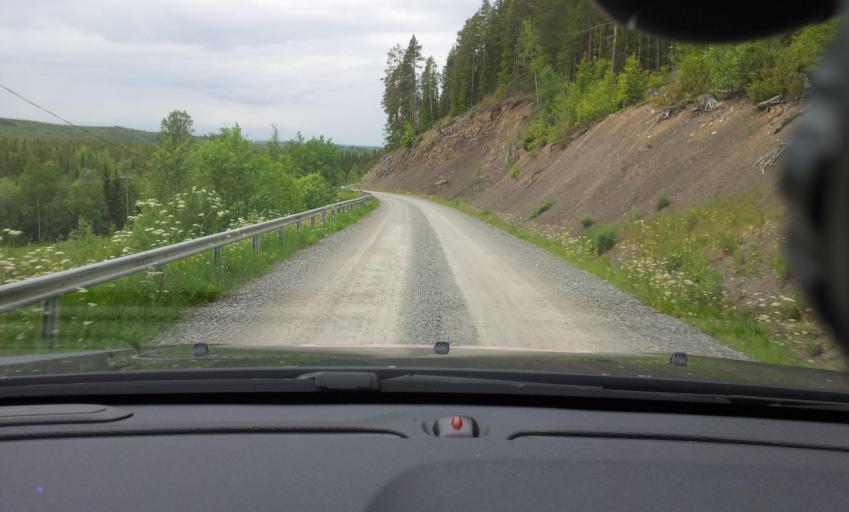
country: SE
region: Jaemtland
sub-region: OEstersunds Kommun
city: Brunflo
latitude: 62.9655
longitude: 14.7051
